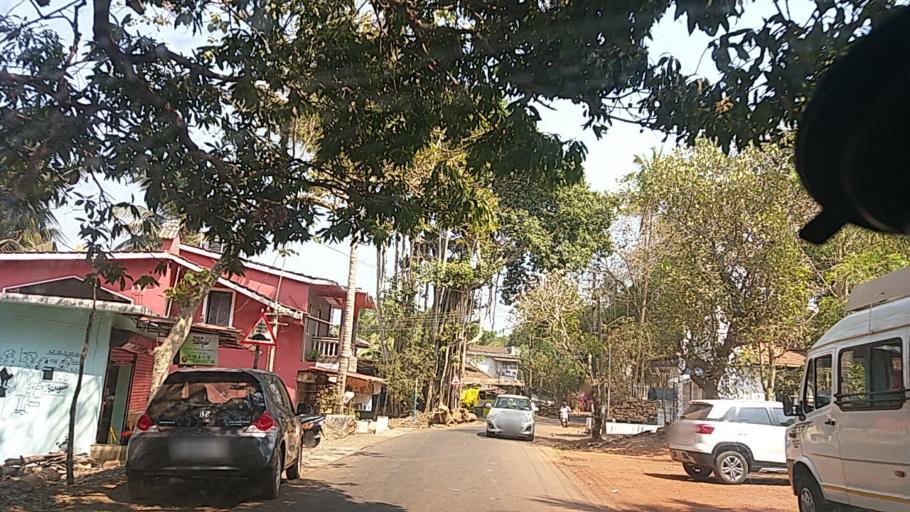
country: IN
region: Goa
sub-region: North Goa
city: Saligao
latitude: 15.5432
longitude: 73.7810
